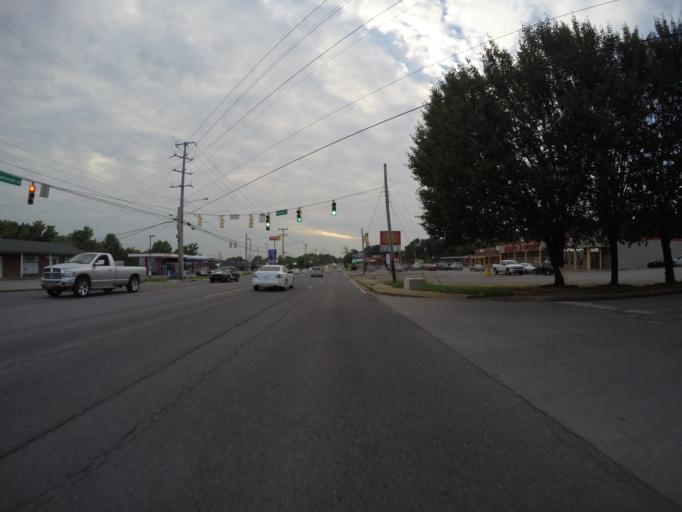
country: US
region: Tennessee
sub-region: Davidson County
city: Lakewood
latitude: 36.2556
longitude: -86.6535
